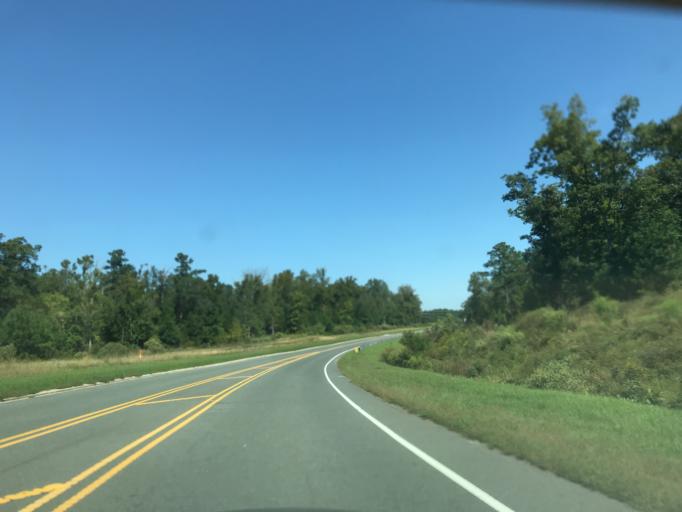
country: US
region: North Carolina
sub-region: Wake County
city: Morrisville
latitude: 35.8687
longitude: -78.8849
